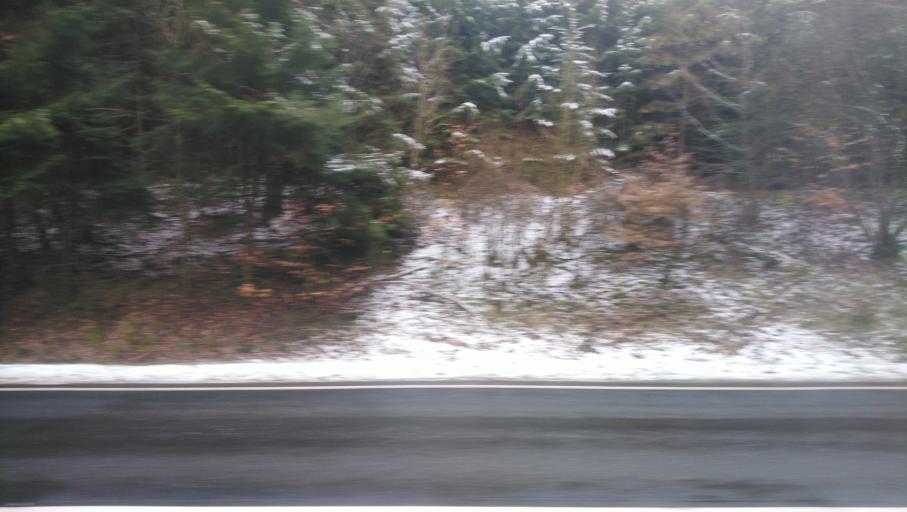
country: LU
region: Grevenmacher
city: Gonderange
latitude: 49.6824
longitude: 6.2235
